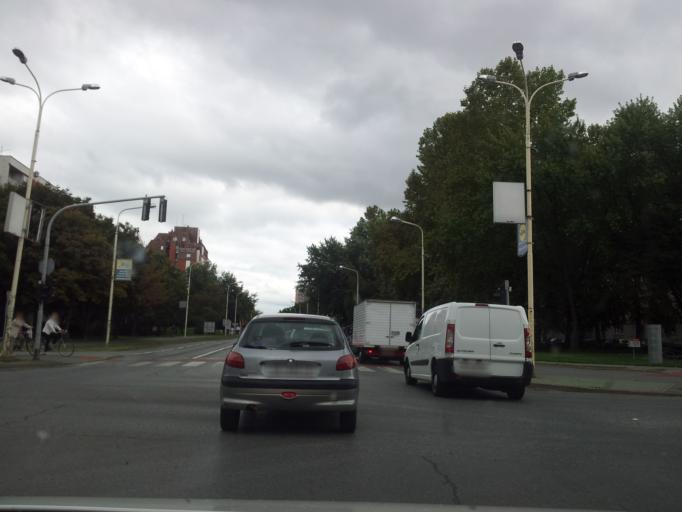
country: HR
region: Osjecko-Baranjska
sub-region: Grad Osijek
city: Osijek
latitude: 45.5549
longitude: 18.6952
